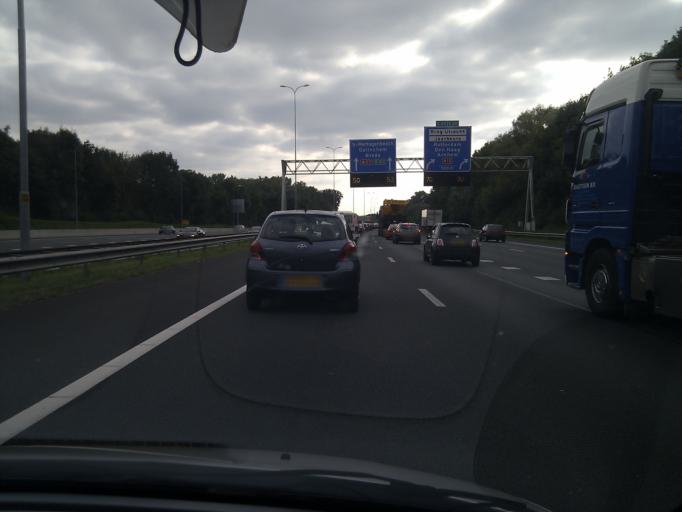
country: NL
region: Utrecht
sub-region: Gemeente Utrecht
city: Lunetten
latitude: 52.0761
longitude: 5.1568
